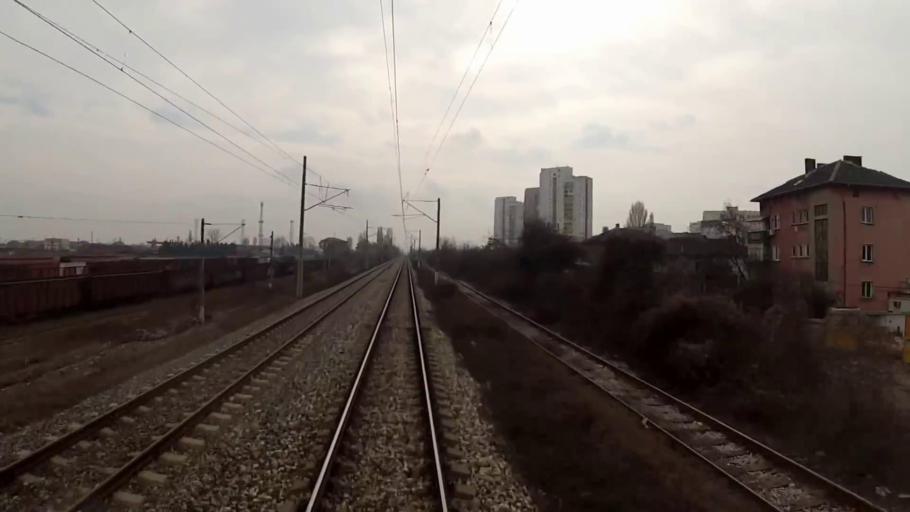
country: BG
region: Sofia-Capital
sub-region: Stolichna Obshtina
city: Sofia
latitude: 42.6734
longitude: 23.3976
